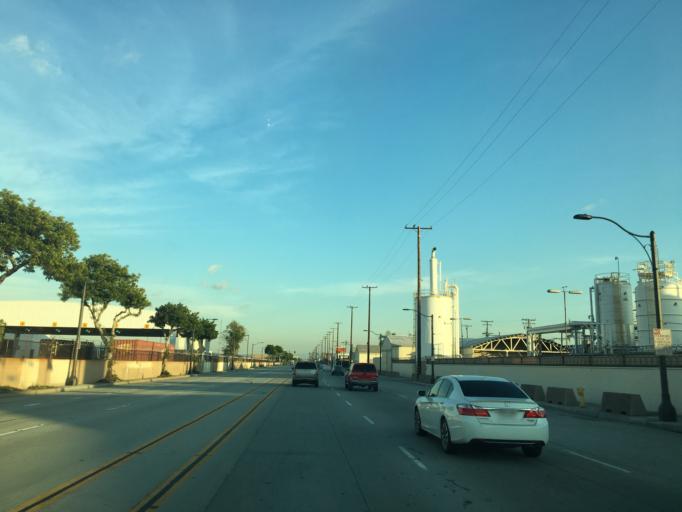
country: US
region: California
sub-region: Los Angeles County
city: East Los Angeles
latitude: 34.0100
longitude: -118.1885
